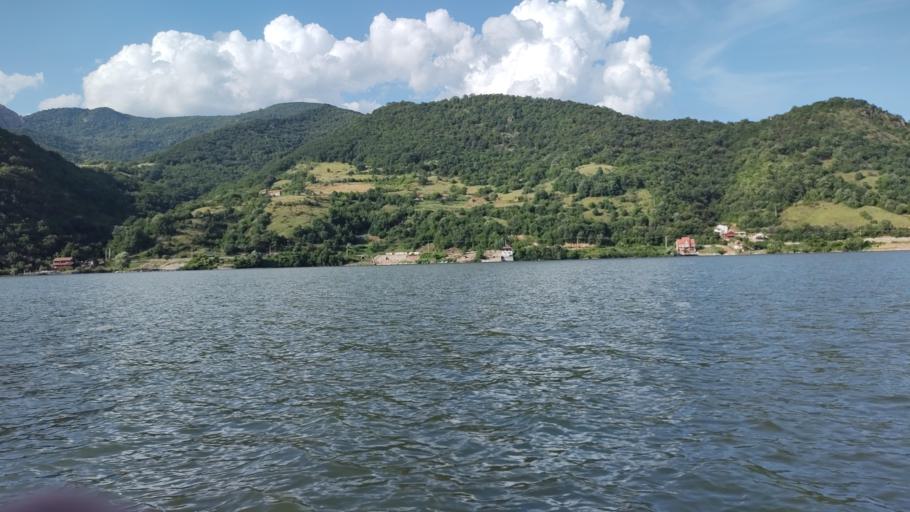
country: RO
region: Mehedinti
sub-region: Comuna Svinita
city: Svinita
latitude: 44.5385
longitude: 22.0562
